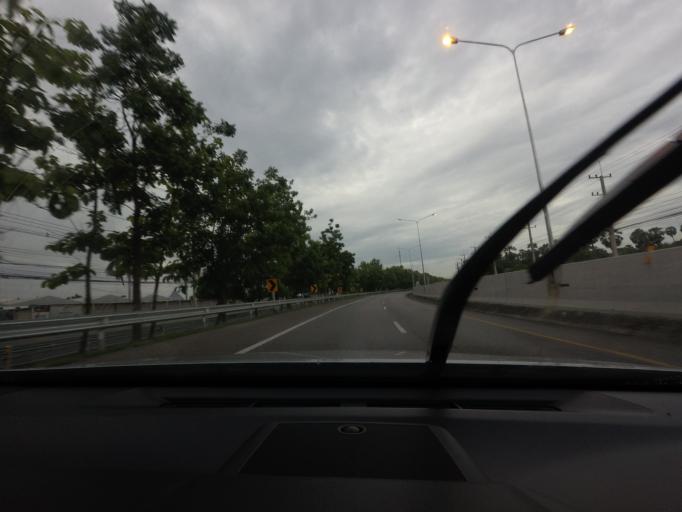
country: TH
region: Phetchaburi
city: Khao Yoi
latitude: 13.2740
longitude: 99.8195
